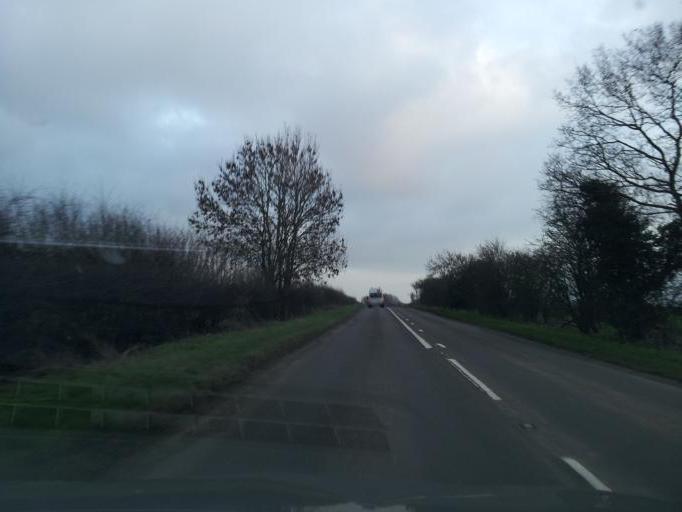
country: GB
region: England
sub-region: Derbyshire
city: Etwall
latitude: 52.8573
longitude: -1.5937
